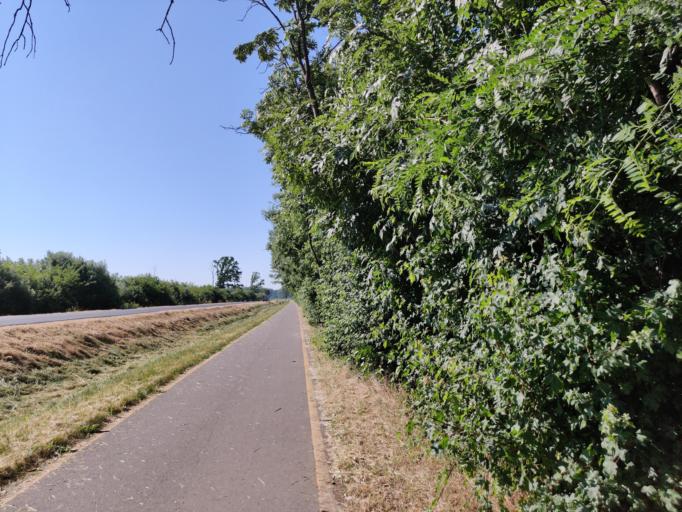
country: HU
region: Hajdu-Bihar
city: Balmazujvaros
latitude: 47.5956
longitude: 21.3397
